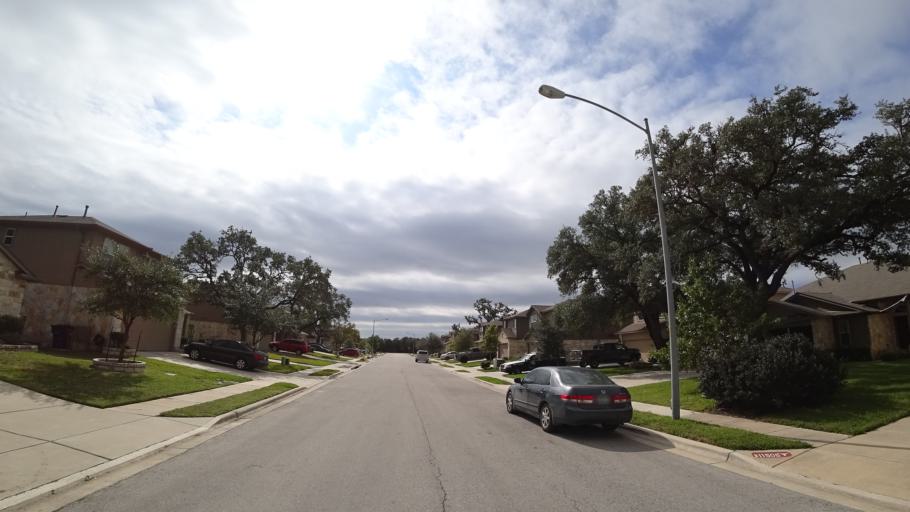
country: US
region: Texas
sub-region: Travis County
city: Manchaca
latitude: 30.1543
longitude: -97.8464
